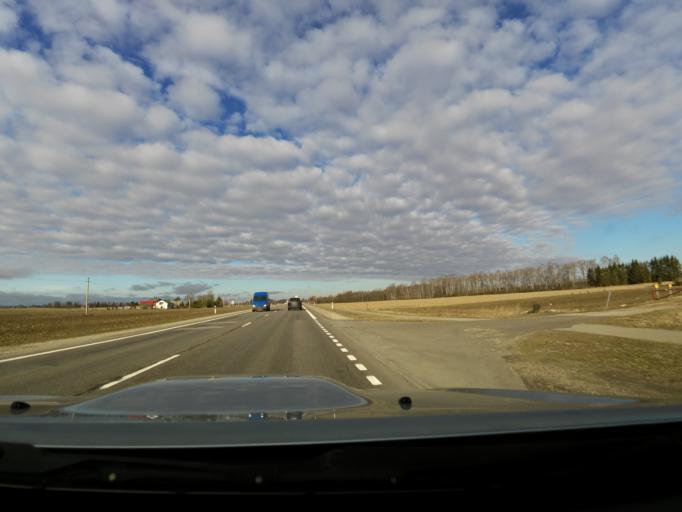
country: LT
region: Panevezys
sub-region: Panevezys City
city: Panevezys
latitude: 55.7398
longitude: 24.1918
